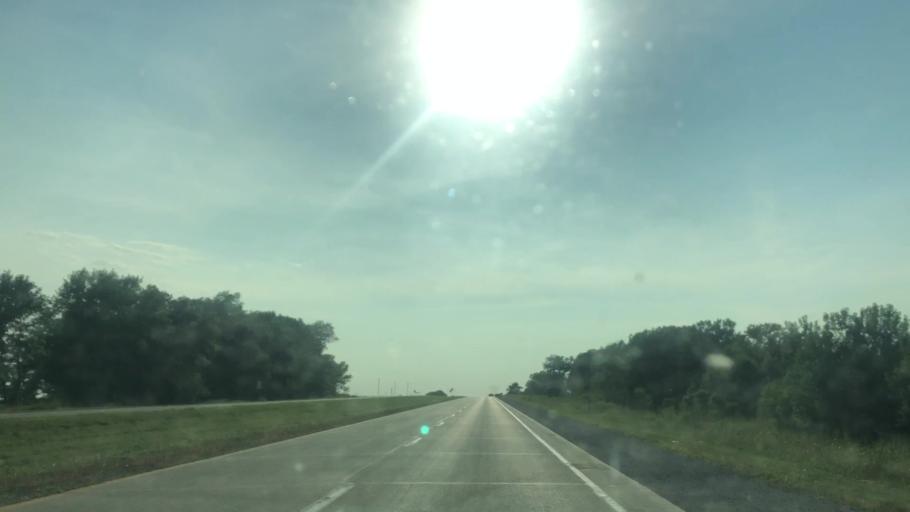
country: US
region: Iowa
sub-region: Story County
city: Nevada
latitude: 42.0078
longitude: -93.3869
